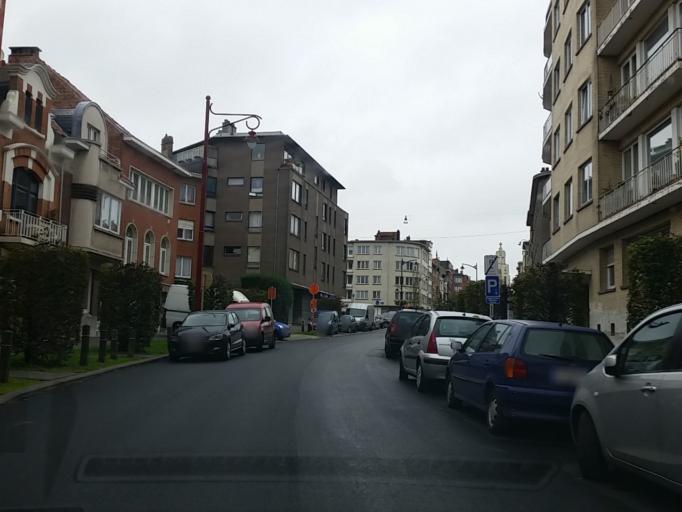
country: BE
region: Flanders
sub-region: Provincie Vlaams-Brabant
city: Drogenbos
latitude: 50.8122
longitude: 4.3352
